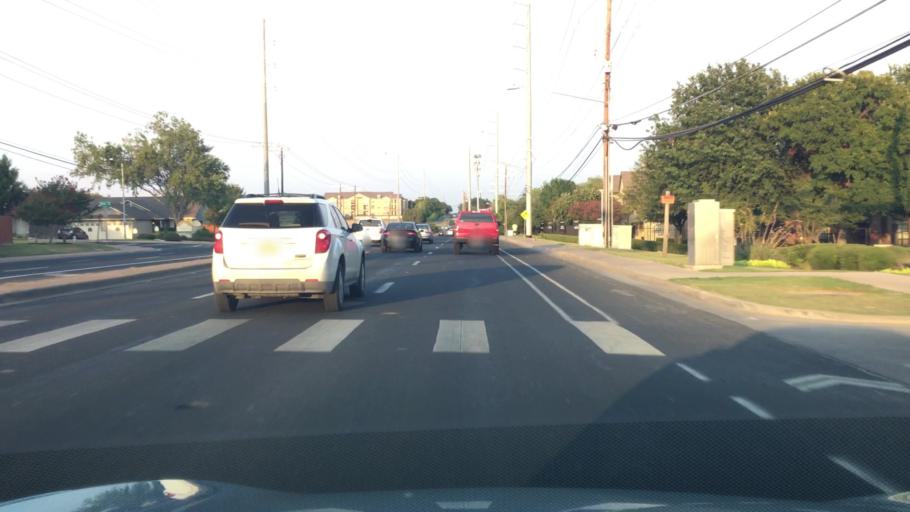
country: US
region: Texas
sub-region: Travis County
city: Manchaca
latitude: 30.1739
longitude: -97.8058
